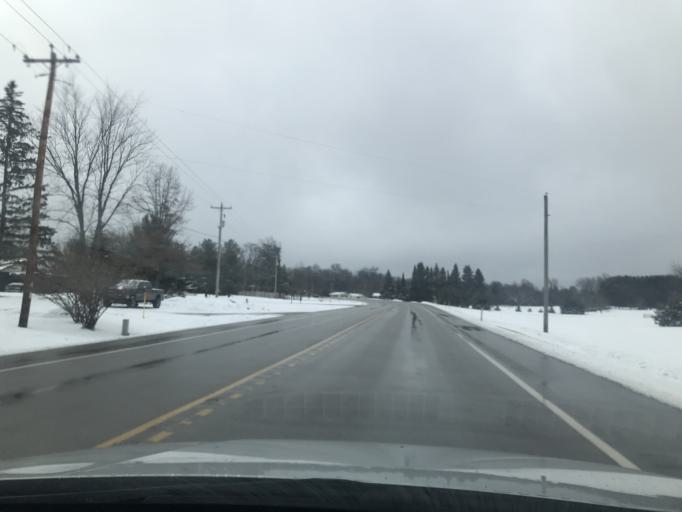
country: US
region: Wisconsin
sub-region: Marinette County
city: Peshtigo
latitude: 45.1756
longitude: -87.7389
